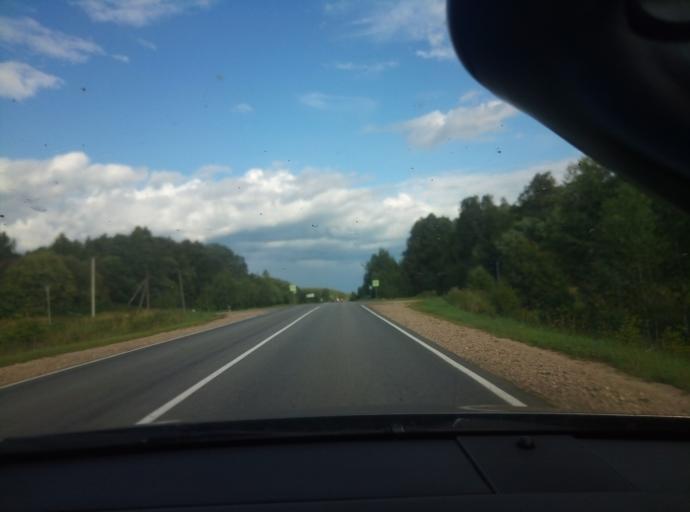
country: RU
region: Kaluga
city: Yukhnov
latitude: 54.5888
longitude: 35.3972
